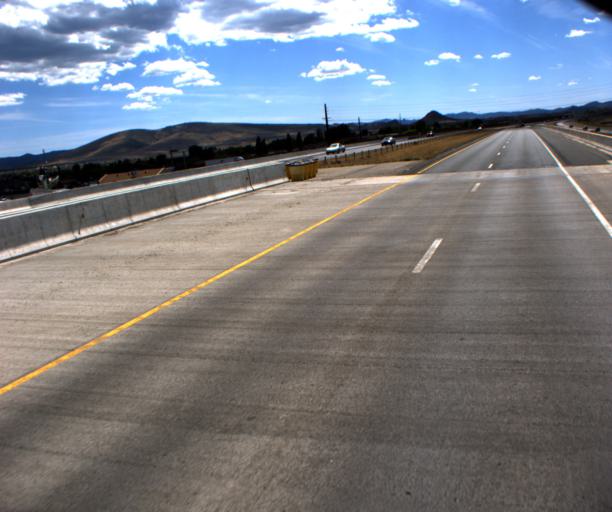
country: US
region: Arizona
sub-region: Yavapai County
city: Prescott Valley
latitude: 34.6368
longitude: -112.3337
